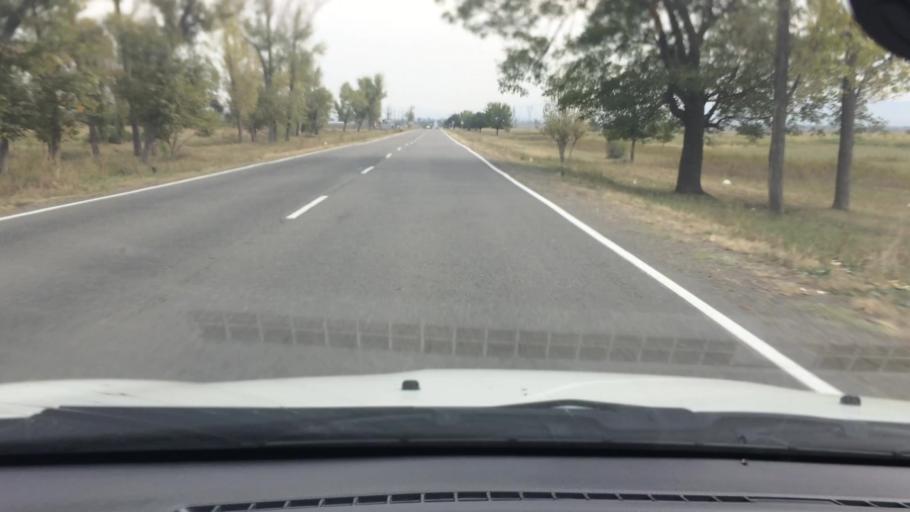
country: GE
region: Kvemo Kartli
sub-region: Gardabani
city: Gardabani
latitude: 41.4444
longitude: 44.9980
